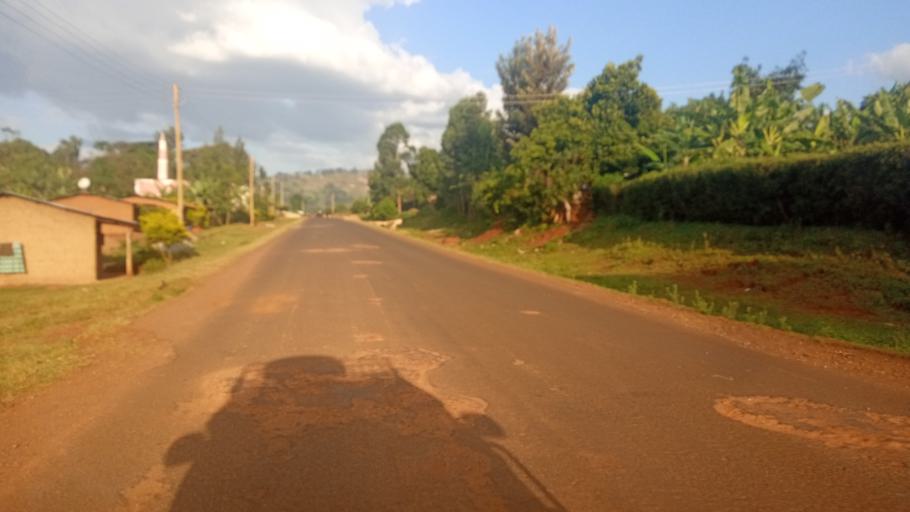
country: UG
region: Eastern Region
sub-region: Kapchorwa District
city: Kapchorwa
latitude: 1.3231
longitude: 34.3483
